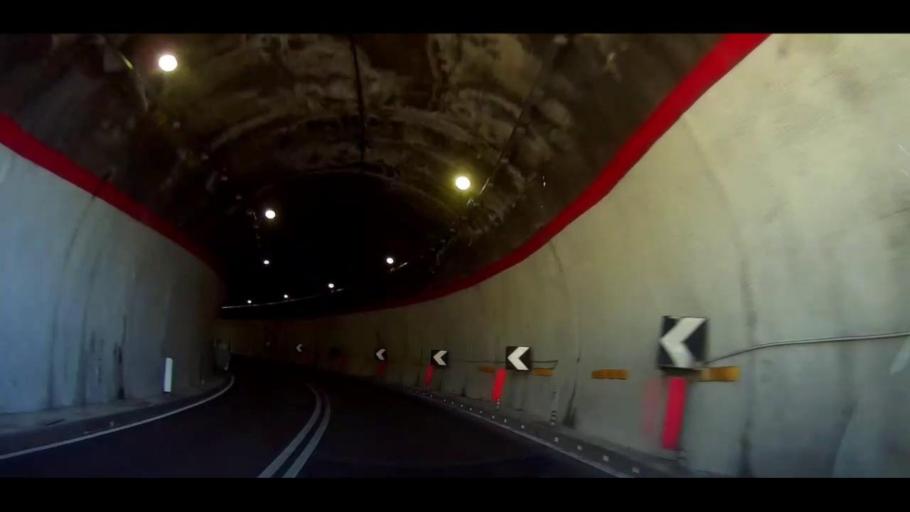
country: IT
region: Calabria
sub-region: Provincia di Cosenza
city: Celico
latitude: 39.3129
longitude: 16.3389
